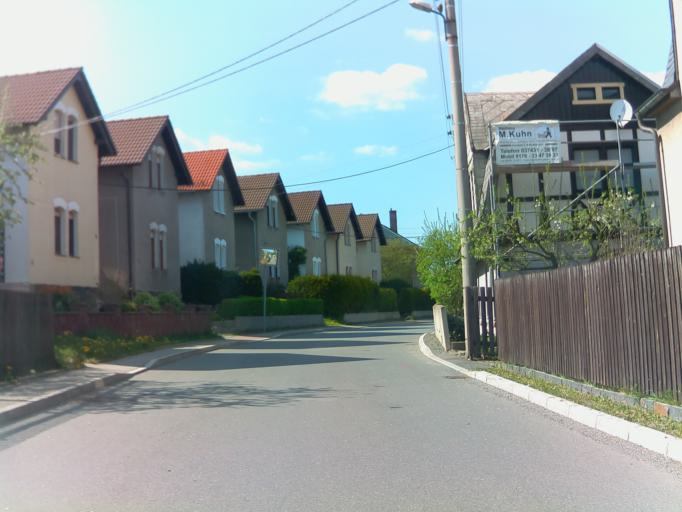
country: DE
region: Saxony
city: Mehltheuer
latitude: 50.5473
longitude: 12.0380
